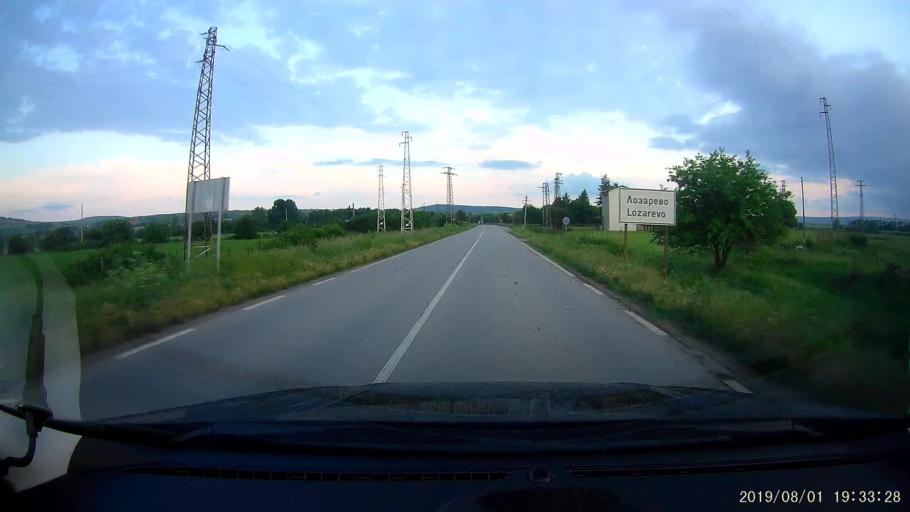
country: BG
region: Burgas
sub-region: Obshtina Sungurlare
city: Sungurlare
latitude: 42.7795
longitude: 26.8767
